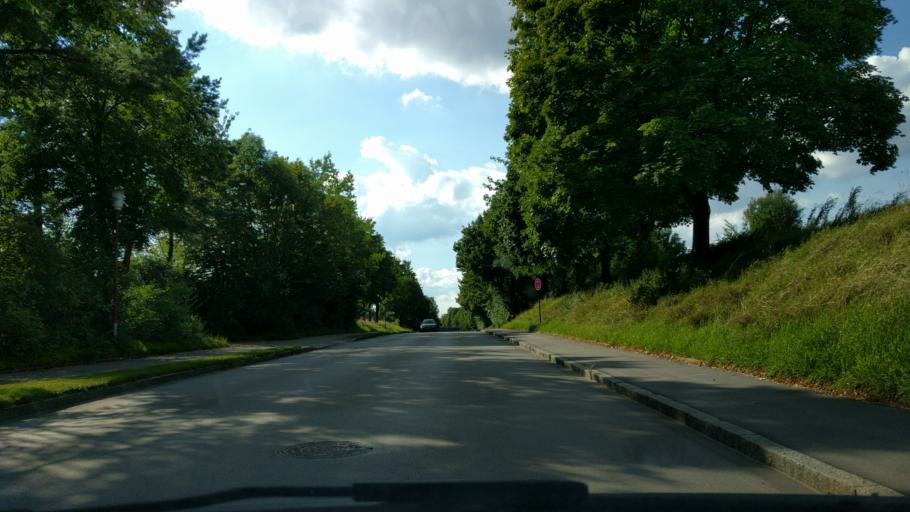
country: DE
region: Bavaria
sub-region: Upper Bavaria
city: Oberhaching
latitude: 48.0270
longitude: 11.5885
